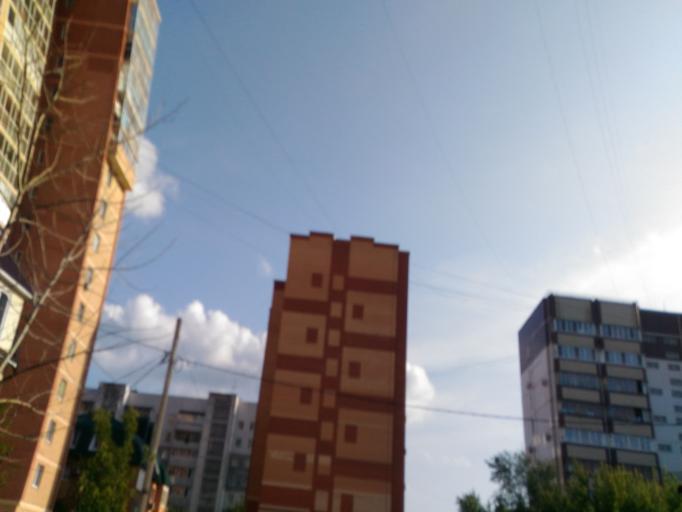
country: RU
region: Ulyanovsk
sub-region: Ulyanovskiy Rayon
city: Ulyanovsk
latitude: 54.3336
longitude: 48.3898
